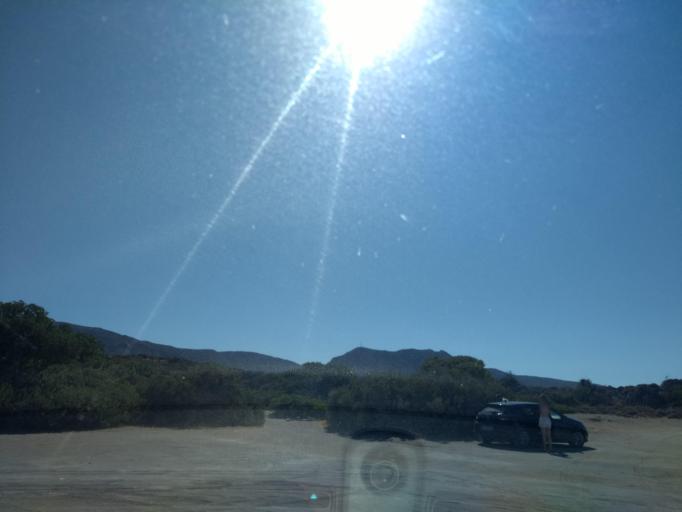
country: GR
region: Crete
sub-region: Nomos Chanias
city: Palaiochora
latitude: 35.2719
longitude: 23.5444
